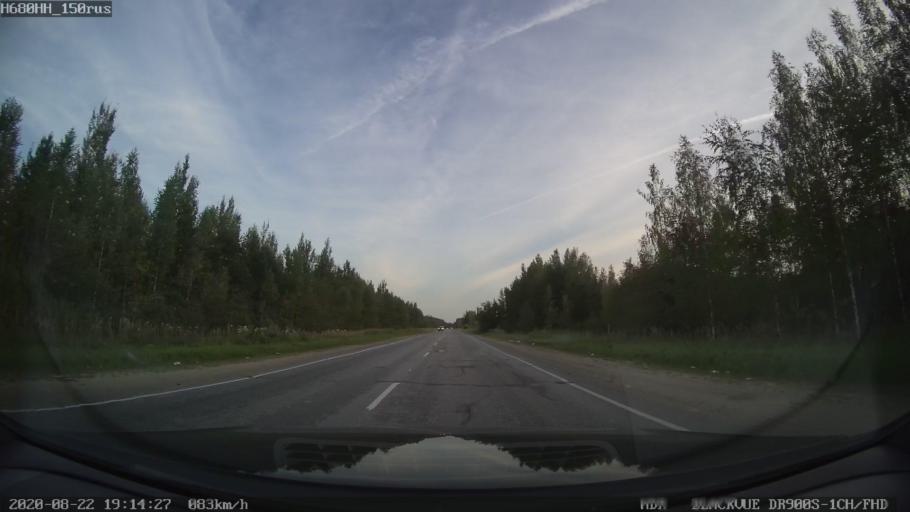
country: RU
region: Tverskaya
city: Sakharovo
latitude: 56.9799
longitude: 36.0235
